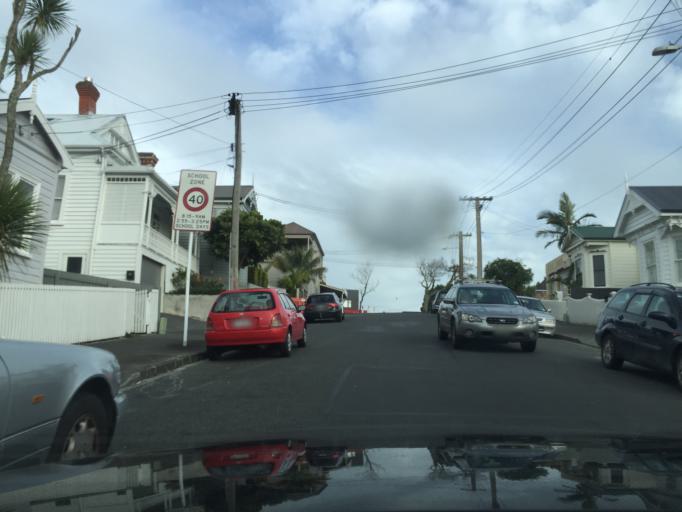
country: NZ
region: Auckland
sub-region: Auckland
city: Auckland
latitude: -36.8547
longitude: 174.7399
